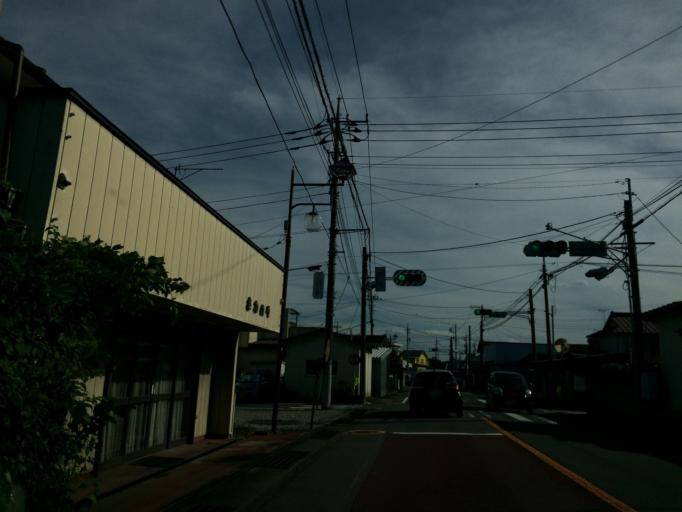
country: JP
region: Gunma
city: Shibukawa
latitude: 36.4978
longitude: 138.9964
